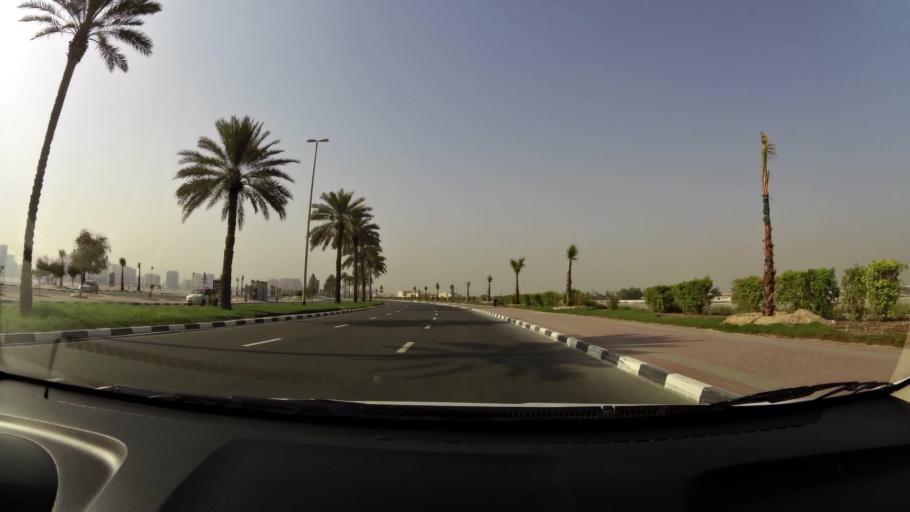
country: AE
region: Ash Shariqah
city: Sharjah
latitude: 25.3058
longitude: 55.3469
